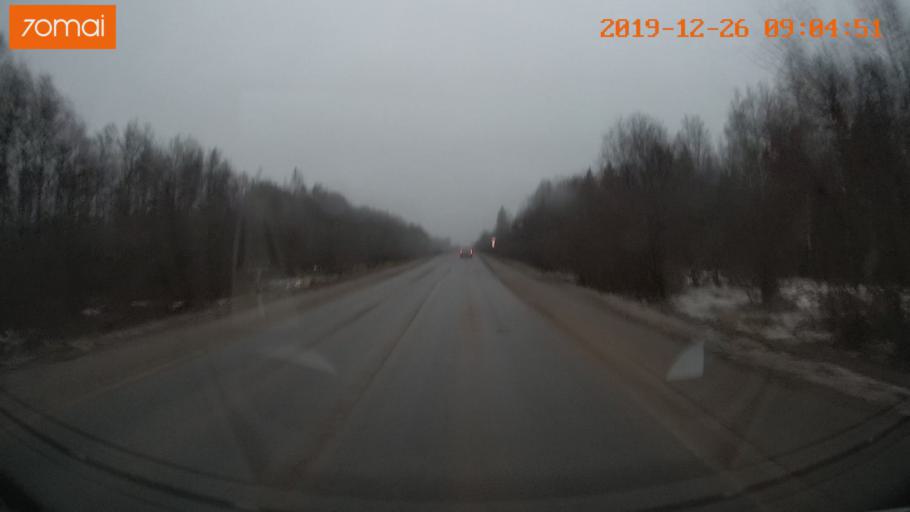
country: RU
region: Vologda
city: Gryazovets
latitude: 58.8194
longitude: 40.2609
